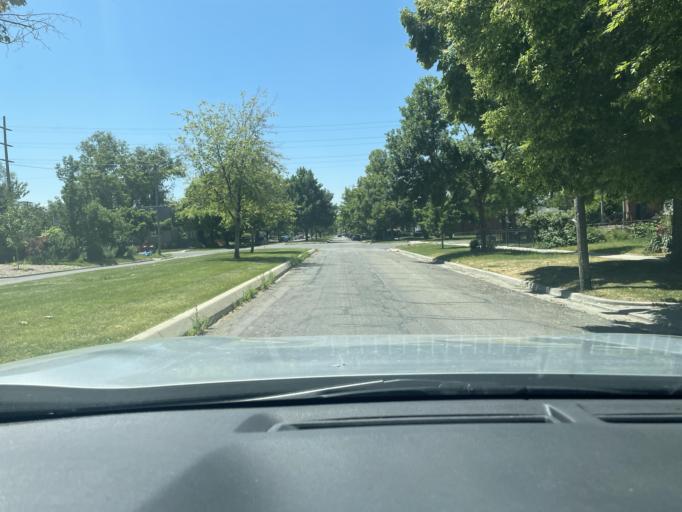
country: US
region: Utah
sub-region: Salt Lake County
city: Salt Lake City
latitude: 40.7548
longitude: -111.8740
